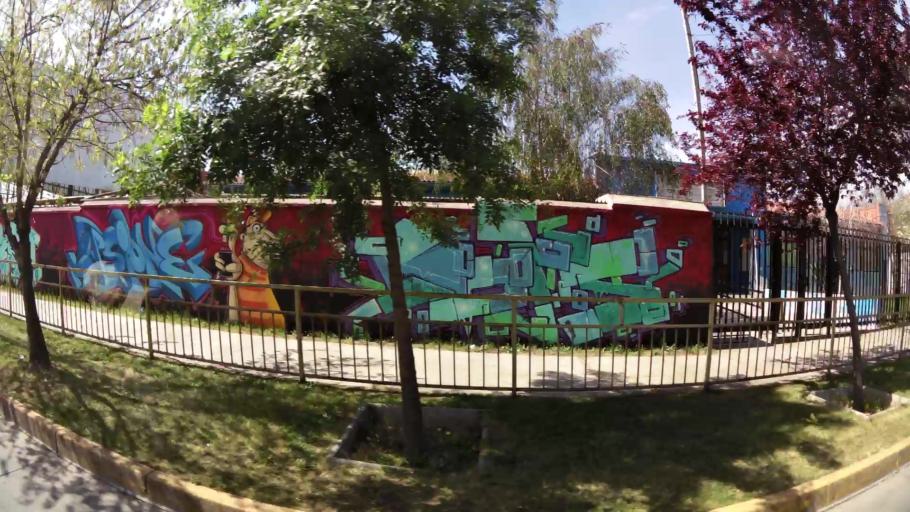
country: CL
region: Santiago Metropolitan
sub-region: Provincia de Cordillera
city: Puente Alto
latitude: -33.5880
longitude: -70.5799
